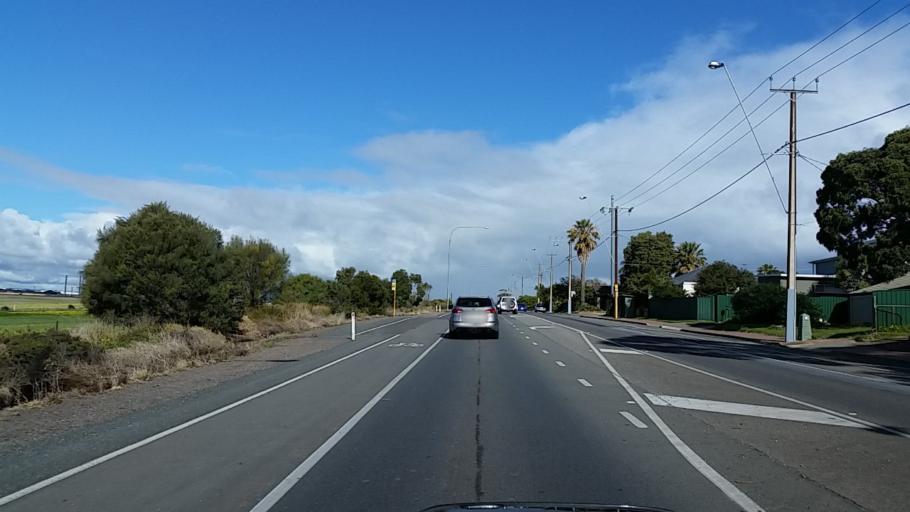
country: AU
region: South Australia
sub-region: Adelaide
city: Port Noarlunga
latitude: -35.1644
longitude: 138.4755
